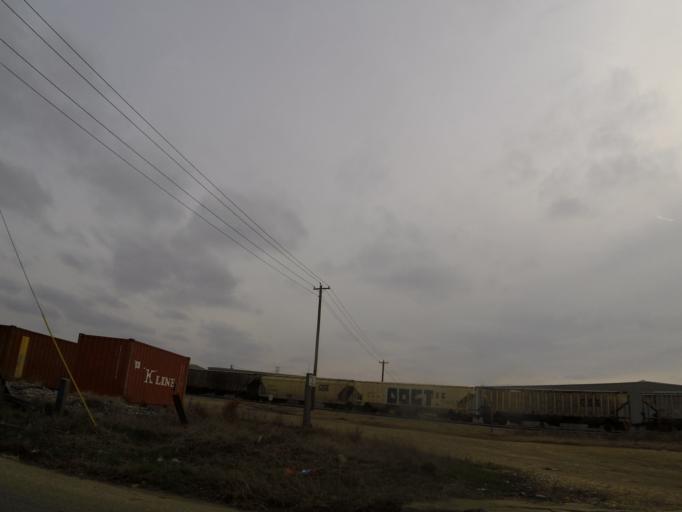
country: US
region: Alabama
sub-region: Montgomery County
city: Montgomery
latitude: 32.3946
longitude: -86.3088
